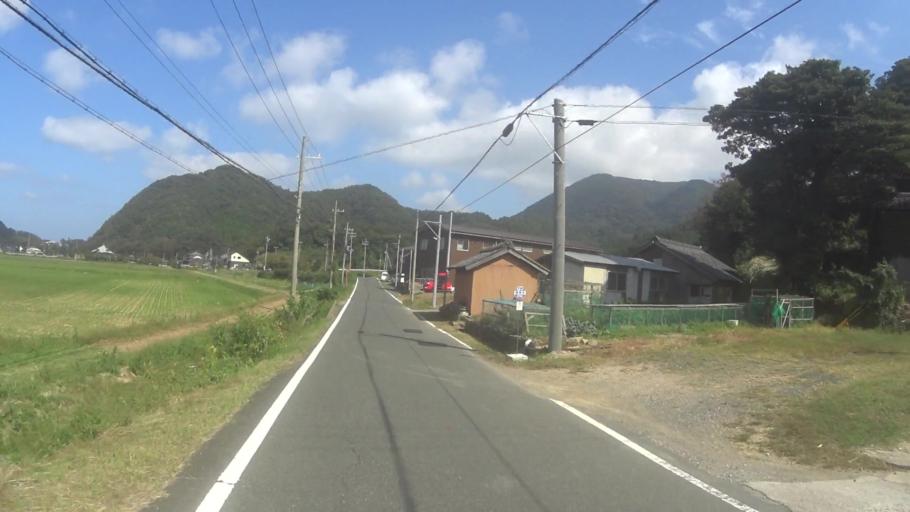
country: JP
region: Kyoto
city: Miyazu
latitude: 35.7326
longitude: 135.1072
